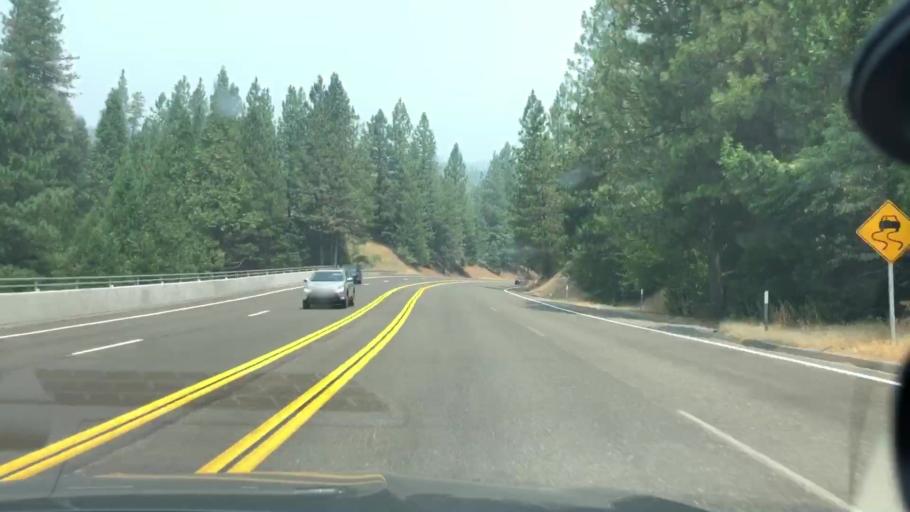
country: US
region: California
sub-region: El Dorado County
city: Pollock Pines
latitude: 38.7694
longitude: -120.4769
